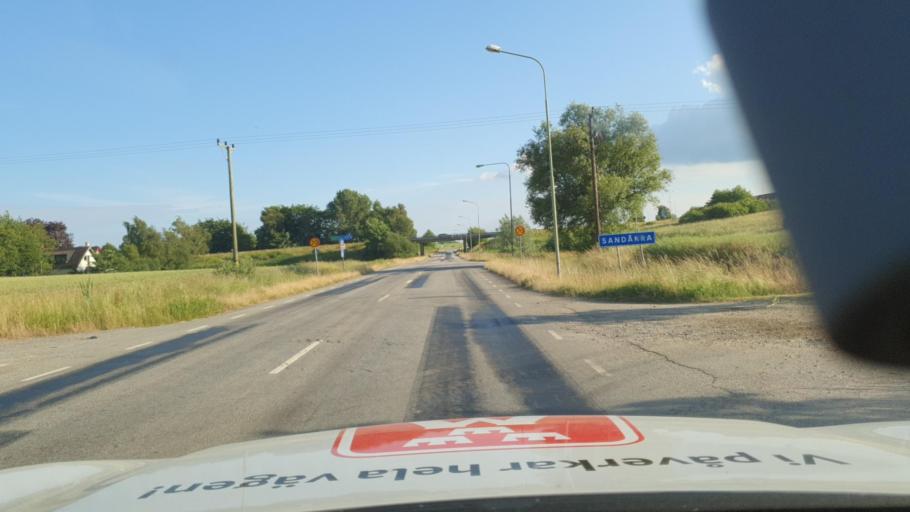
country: SE
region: Skane
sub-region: Skurups Kommun
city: Skurup
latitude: 55.4966
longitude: 13.5099
